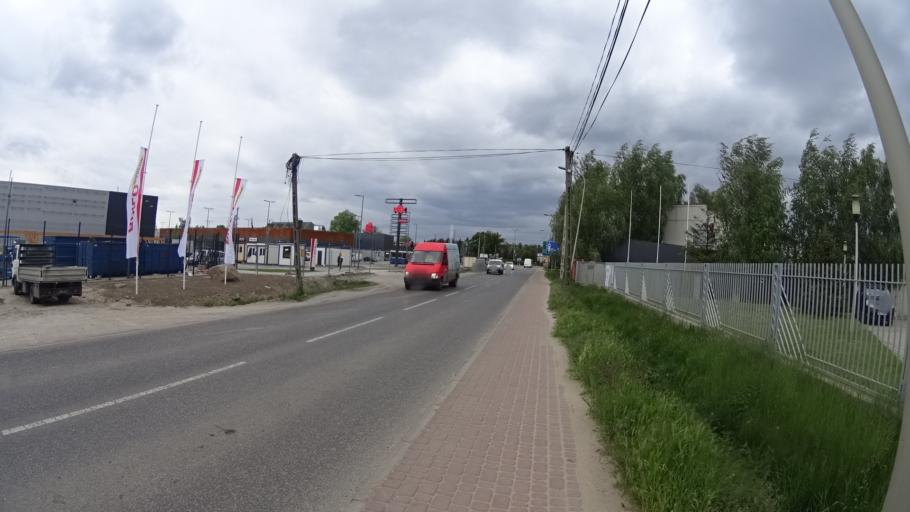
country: PL
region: Masovian Voivodeship
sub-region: Powiat warszawski zachodni
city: Babice
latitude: 52.2464
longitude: 20.8482
